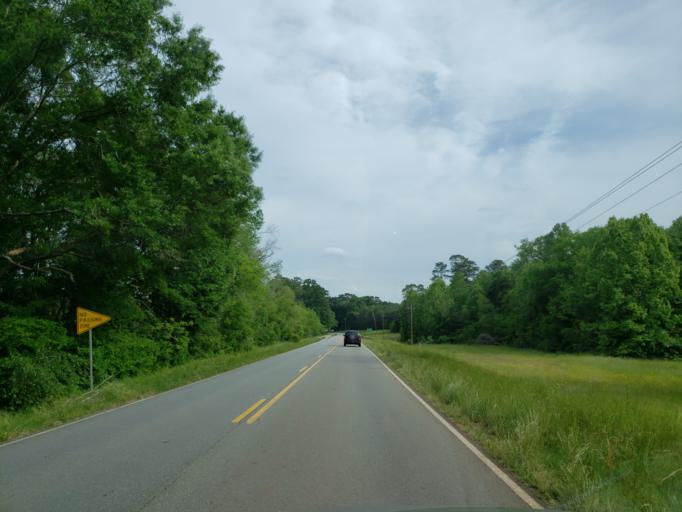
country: US
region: Georgia
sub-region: Dooly County
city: Vienna
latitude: 32.1189
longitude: -83.8632
